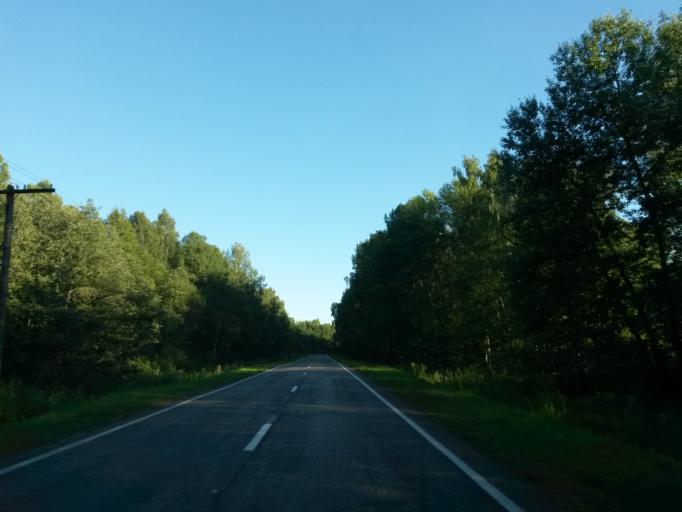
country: RU
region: Jaroslavl
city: Tutayev
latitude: 57.9205
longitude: 39.5135
